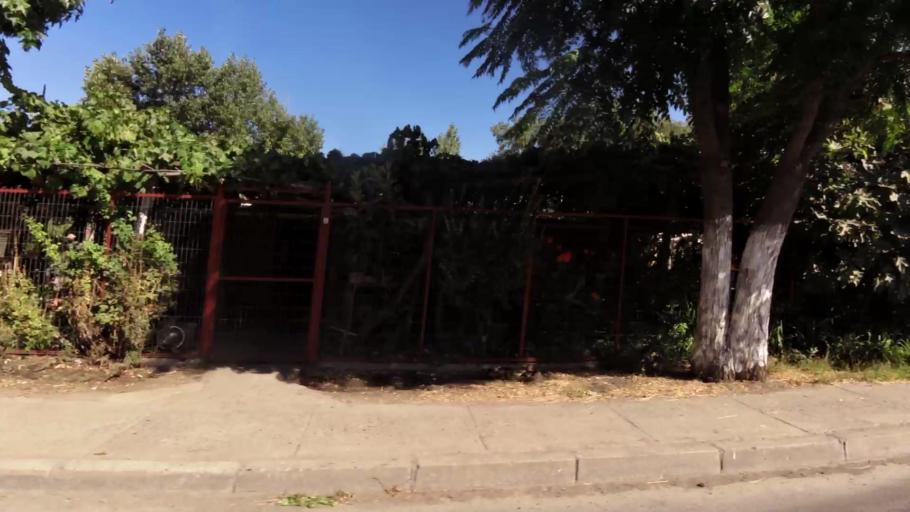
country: CL
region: Maule
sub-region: Provincia de Talca
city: Talca
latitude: -35.3985
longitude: -71.6257
